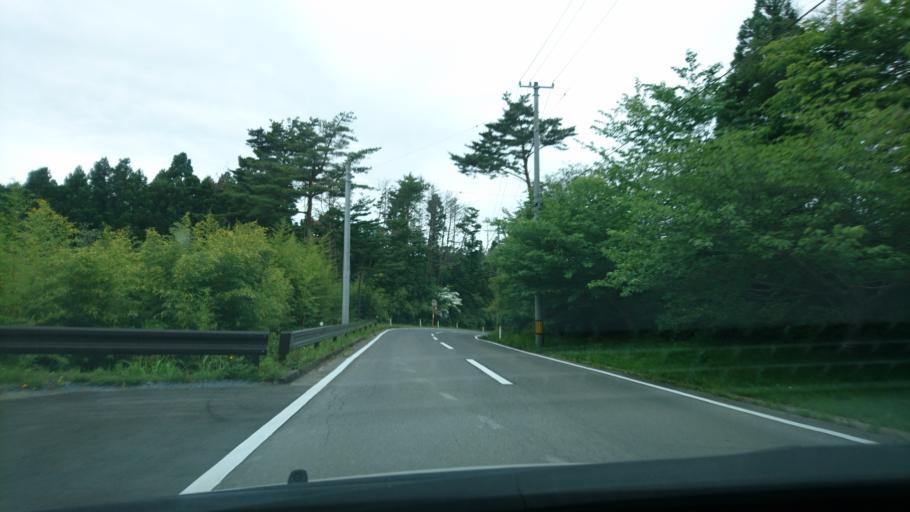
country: JP
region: Miyagi
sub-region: Oshika Gun
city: Onagawa Cho
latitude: 38.7769
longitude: 141.5160
